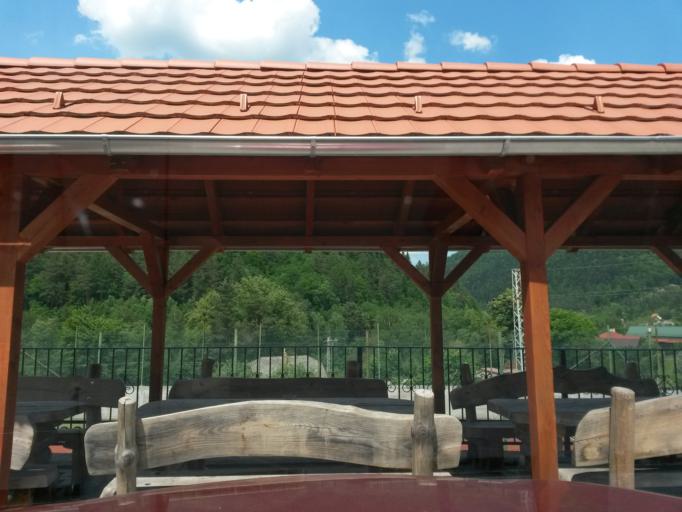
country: SK
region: Kosicky
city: Gelnica
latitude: 48.8136
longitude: 20.9134
